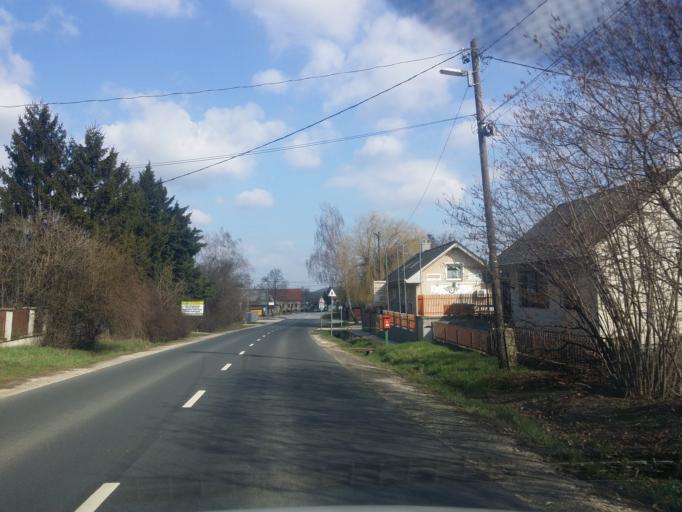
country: HU
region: Fejer
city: Many
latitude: 47.5901
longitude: 18.6648
